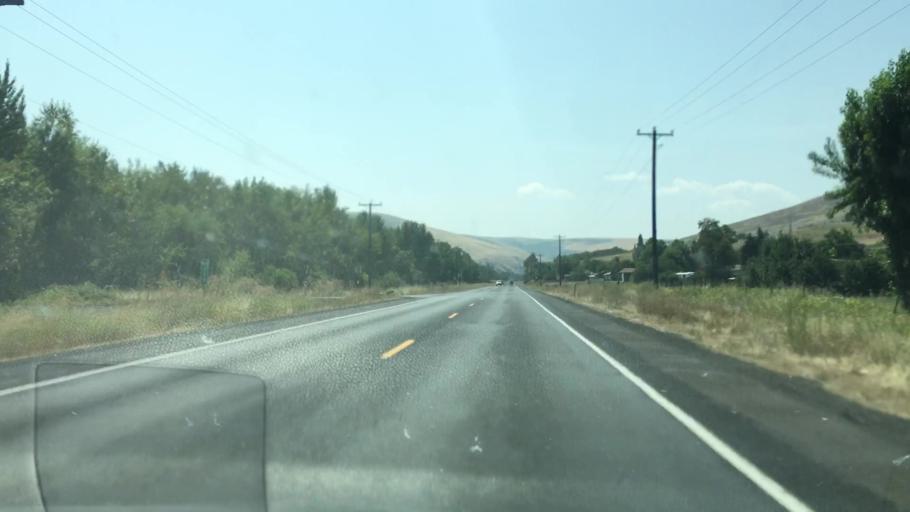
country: US
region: Idaho
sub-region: Nez Perce County
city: Lapwai
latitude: 46.3945
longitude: -116.7991
